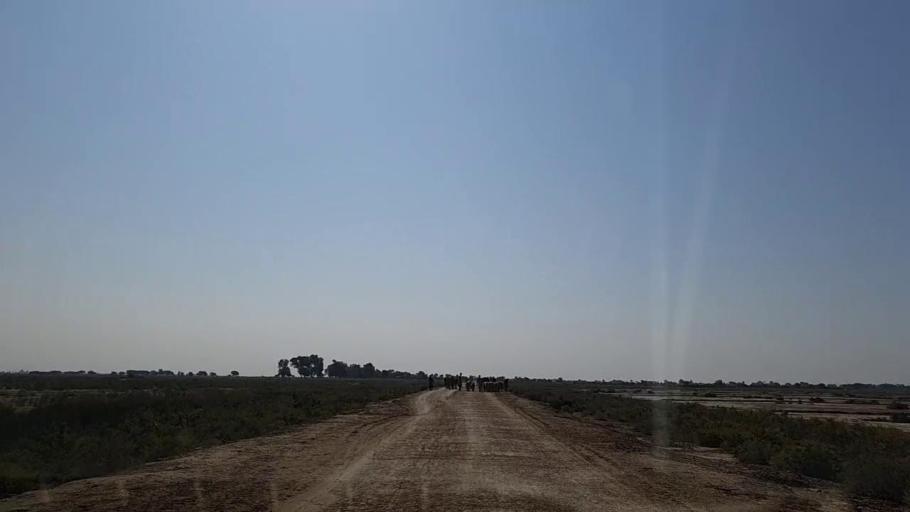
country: PK
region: Sindh
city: Chuhar Jamali
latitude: 24.5034
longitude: 68.0983
